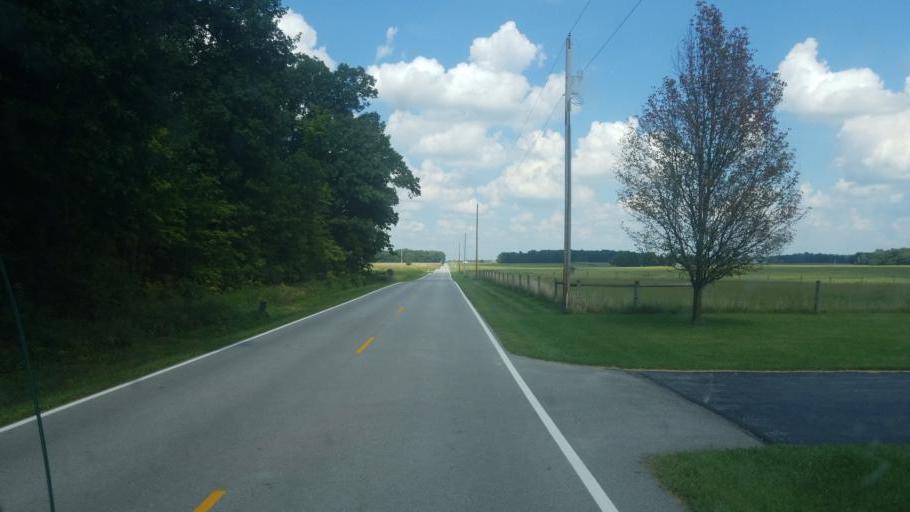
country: US
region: Ohio
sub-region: Hancock County
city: Arlington
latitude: 40.8548
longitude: -83.7277
